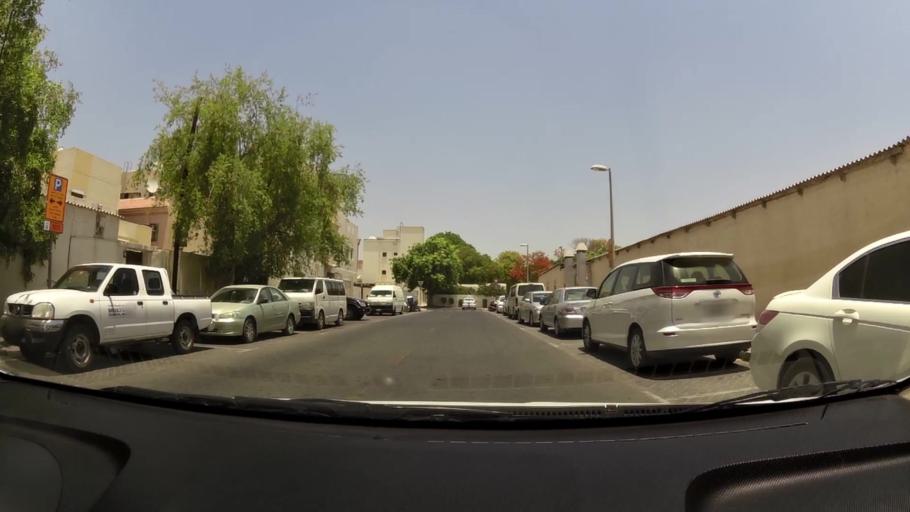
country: AE
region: Ash Shariqah
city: Sharjah
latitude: 25.2731
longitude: 55.3350
